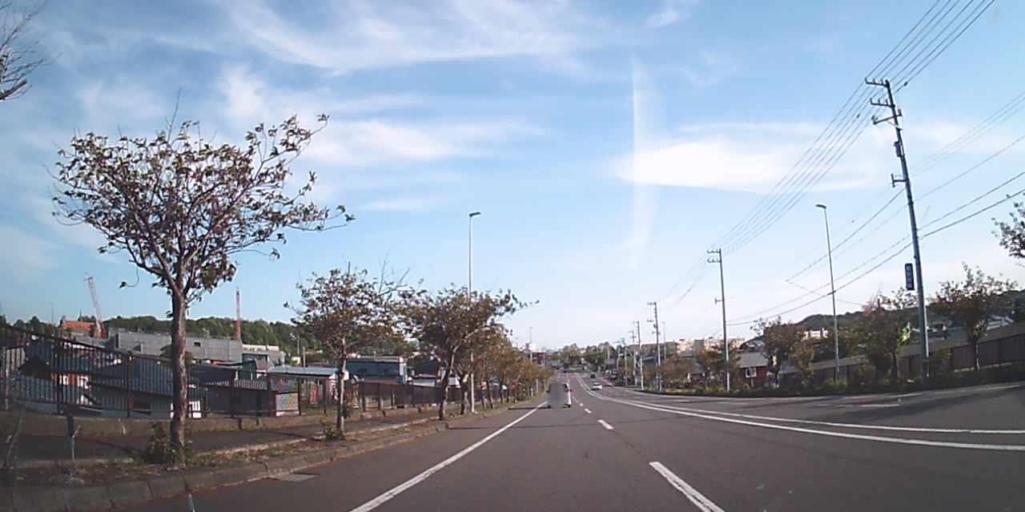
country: JP
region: Hokkaido
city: Shiraoi
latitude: 42.4590
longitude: 141.1776
